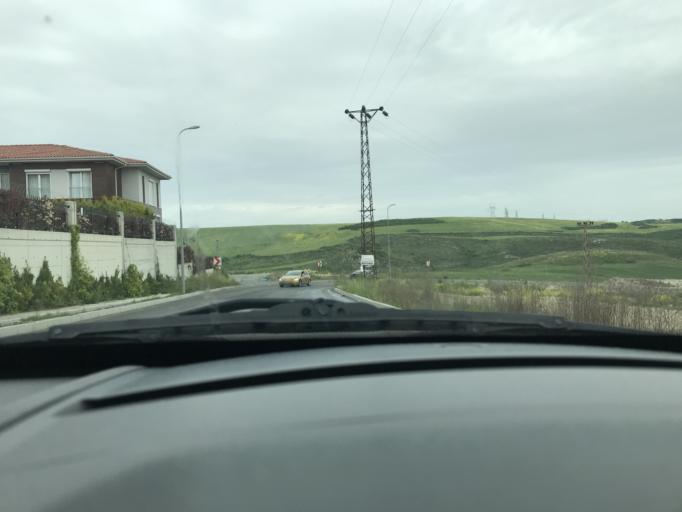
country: TR
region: Istanbul
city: Esenyurt
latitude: 41.0964
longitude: 28.6800
